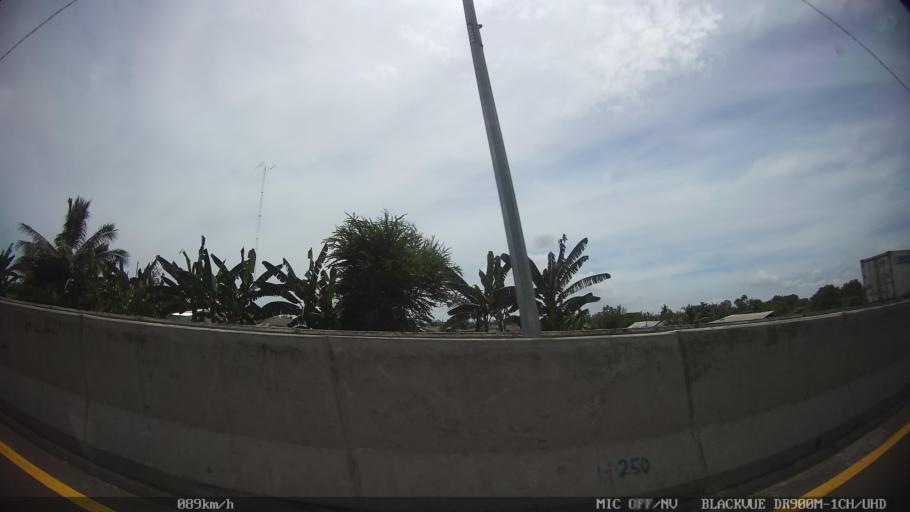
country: ID
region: North Sumatra
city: Belawan
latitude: 3.7566
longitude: 98.6827
